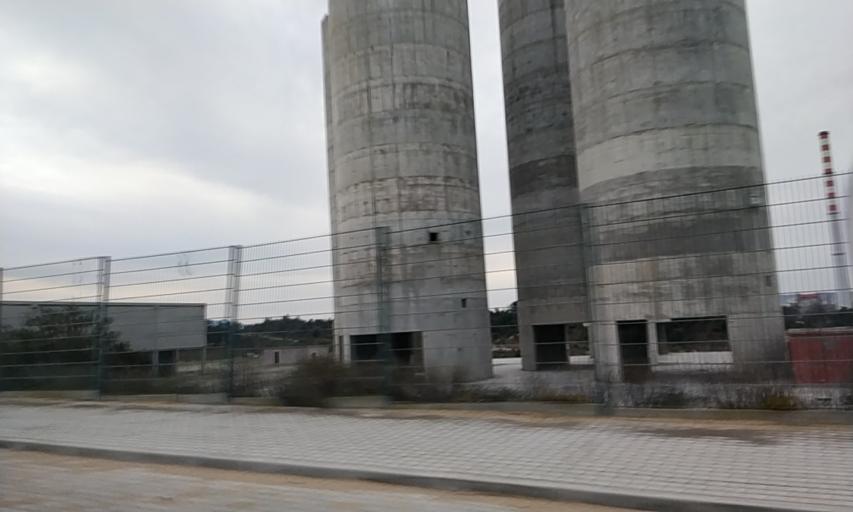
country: PT
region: Setubal
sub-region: Setubal
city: Setubal
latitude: 38.5047
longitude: -8.8380
